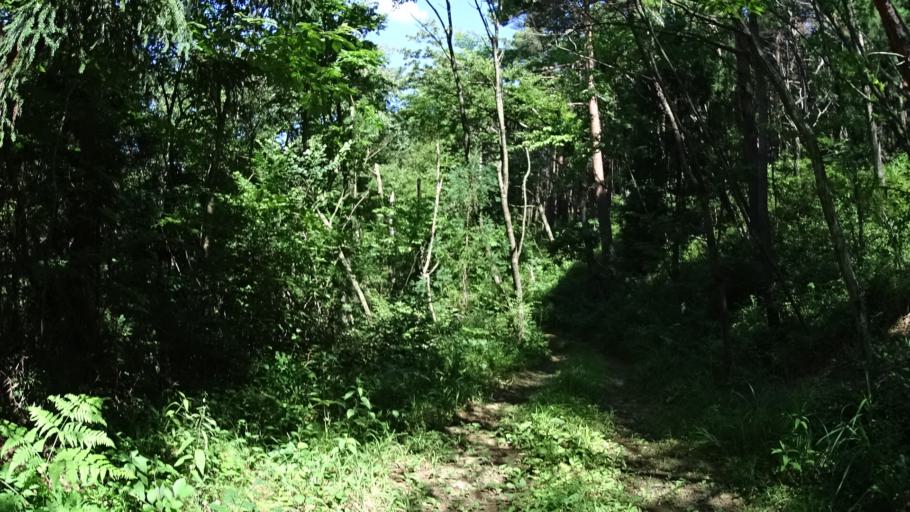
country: JP
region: Iwate
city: Ofunato
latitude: 38.8725
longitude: 141.6131
